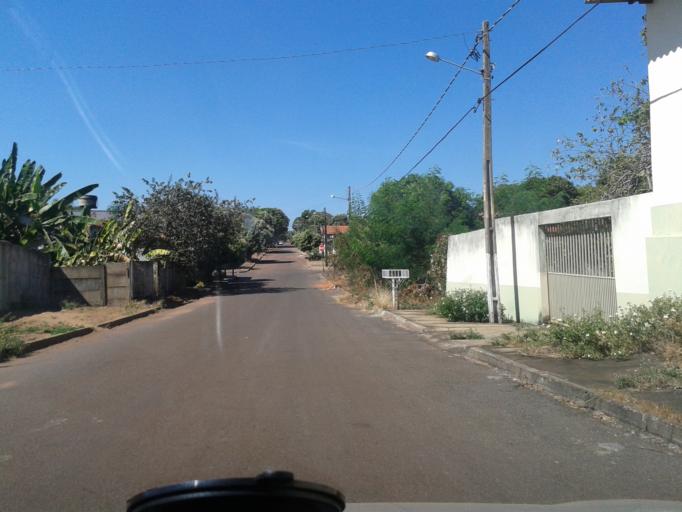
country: BR
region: Goias
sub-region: Sao Miguel Do Araguaia
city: Sao Miguel do Araguaia
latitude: -13.2796
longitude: -50.1568
